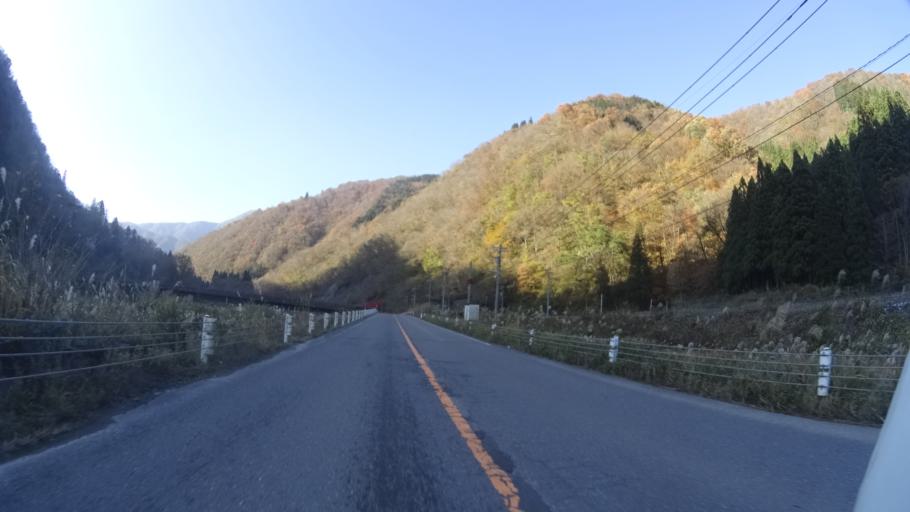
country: JP
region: Fukui
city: Ono
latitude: 35.9033
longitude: 136.6487
